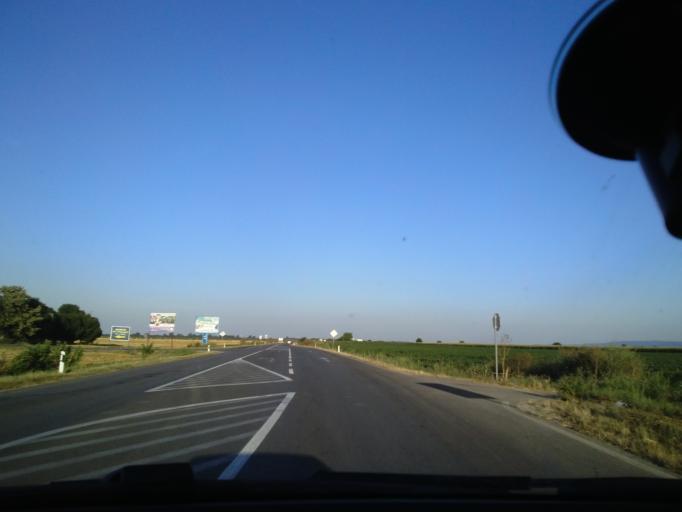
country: RS
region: Autonomna Pokrajina Vojvodina
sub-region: Juznobacki Okrug
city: Backi Petrovac
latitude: 45.3486
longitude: 19.6209
